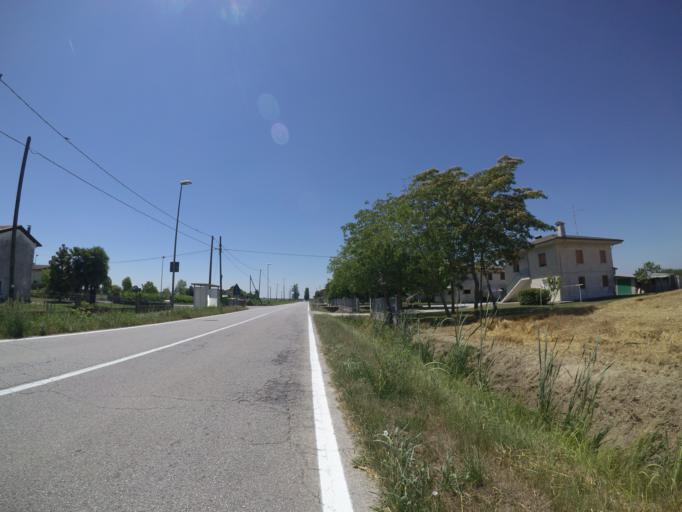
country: IT
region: Friuli Venezia Giulia
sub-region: Provincia di Udine
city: Teor
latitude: 45.8492
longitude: 13.0330
